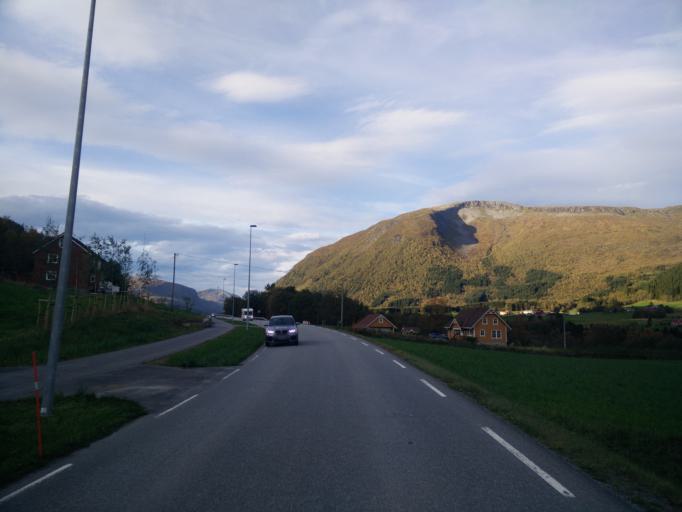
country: NO
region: More og Romsdal
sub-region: Gjemnes
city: Batnfjordsora
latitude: 62.8860
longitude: 7.6708
